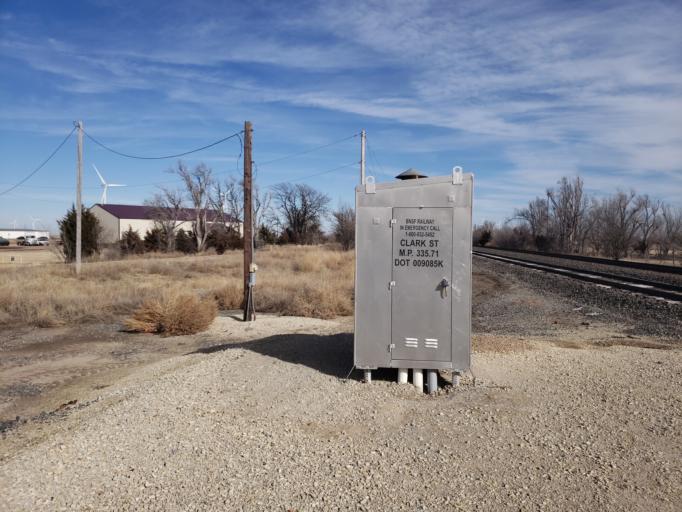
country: US
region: Kansas
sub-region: Hodgeman County
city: Jetmore
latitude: 37.8534
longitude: -99.7531
